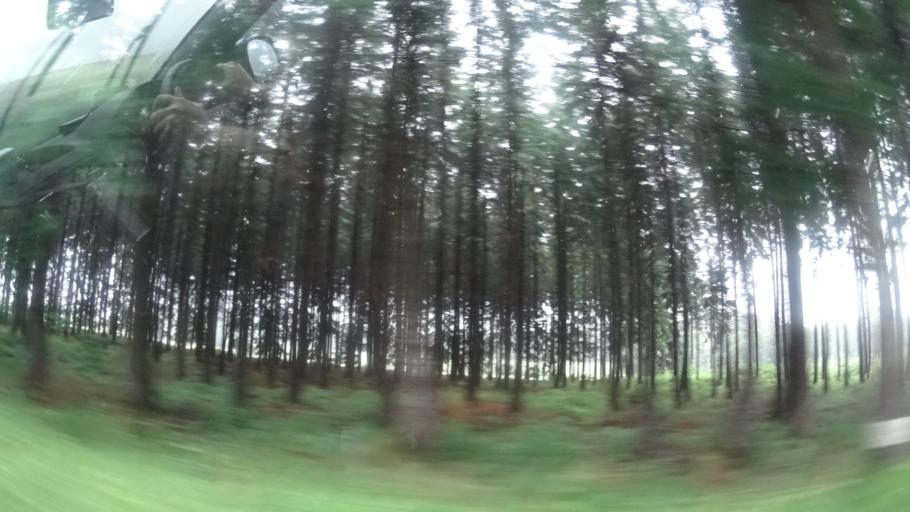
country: BE
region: Wallonia
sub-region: Province du Luxembourg
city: Bertrix
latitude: 49.8482
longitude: 5.3019
